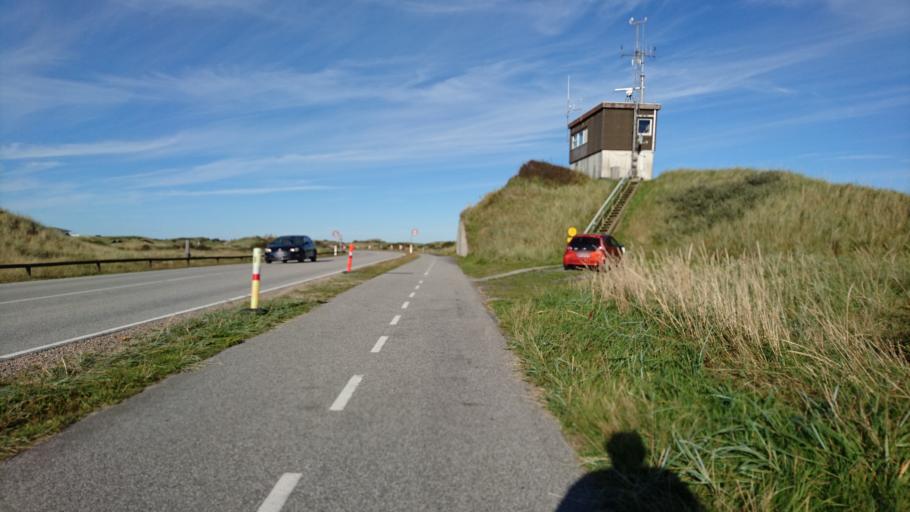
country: DK
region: North Denmark
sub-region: Frederikshavn Kommune
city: Skagen
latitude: 57.7365
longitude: 10.6311
